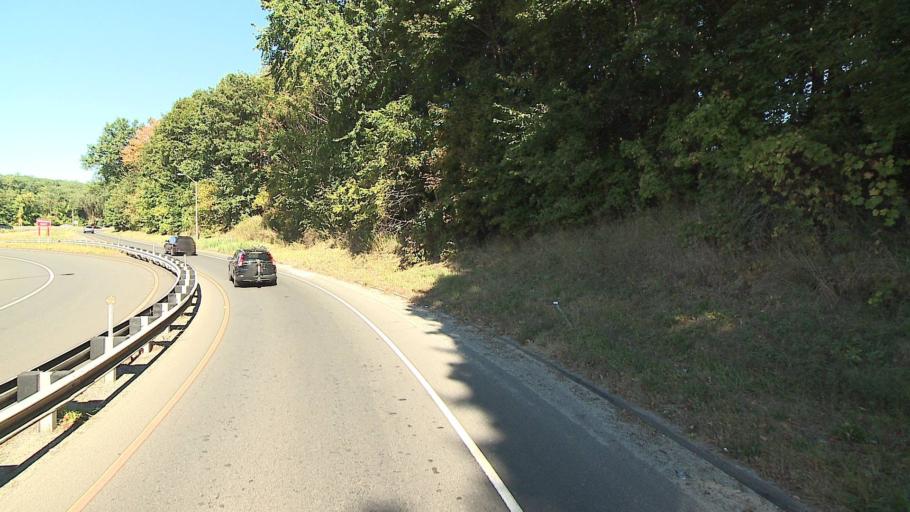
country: US
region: Connecticut
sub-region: Fairfield County
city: Danbury
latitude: 41.3908
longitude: -73.4751
